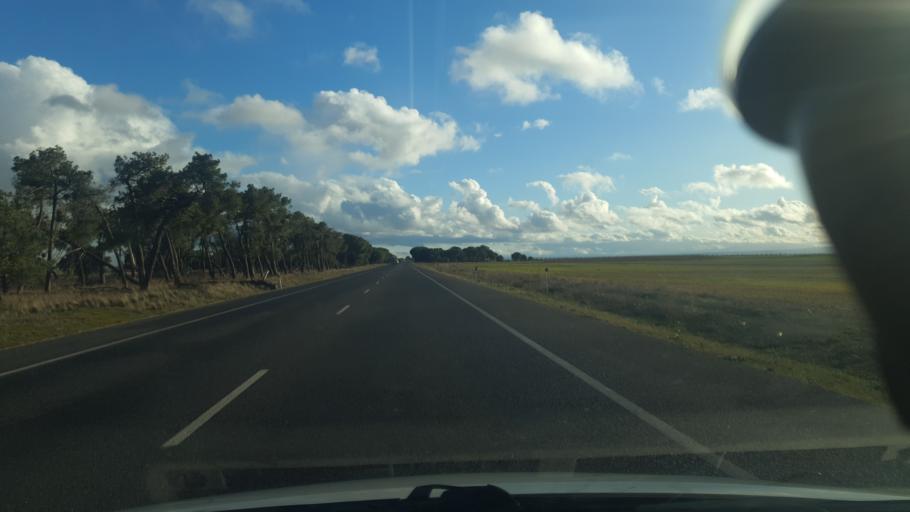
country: ES
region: Castille and Leon
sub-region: Provincia de Segovia
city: Rapariegos
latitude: 41.0713
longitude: -4.6334
